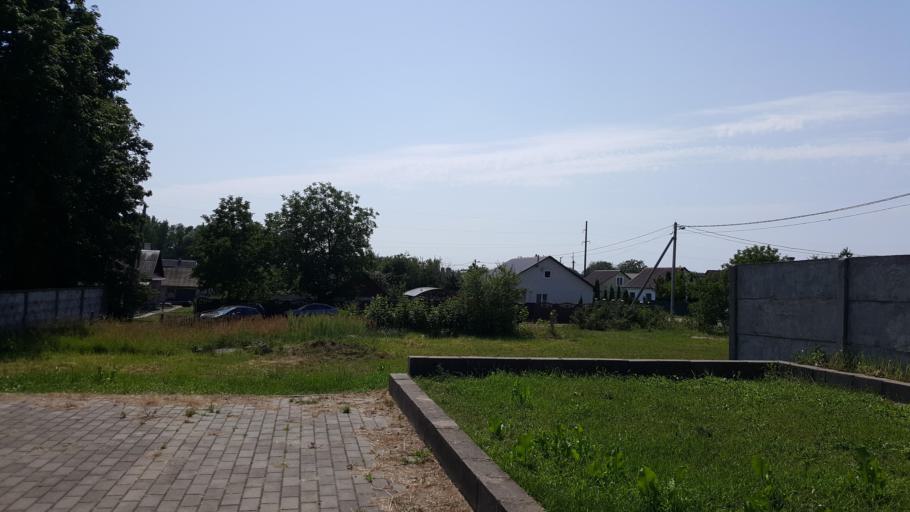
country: BY
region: Brest
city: Zhabinka
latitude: 52.1927
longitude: 24.0161
